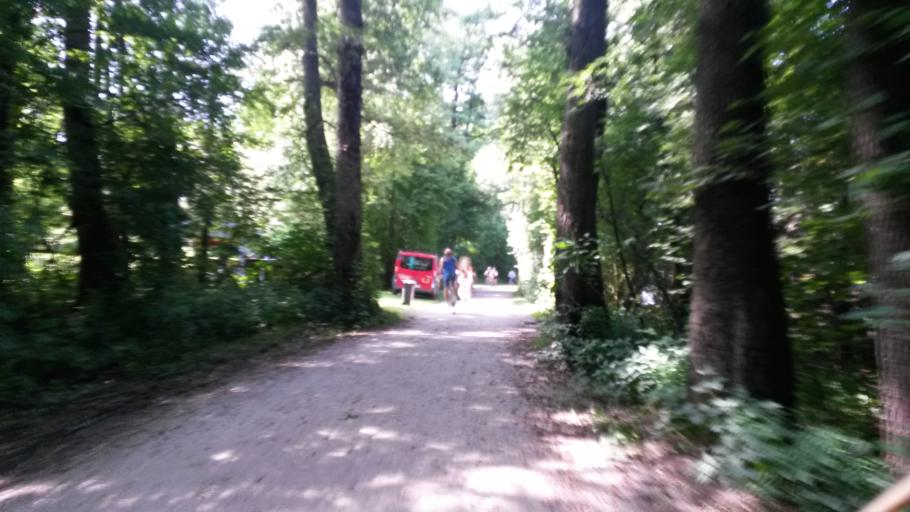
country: DE
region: Bavaria
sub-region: Upper Bavaria
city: Gstadt am Chiemsee
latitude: 47.8815
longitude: 12.3991
